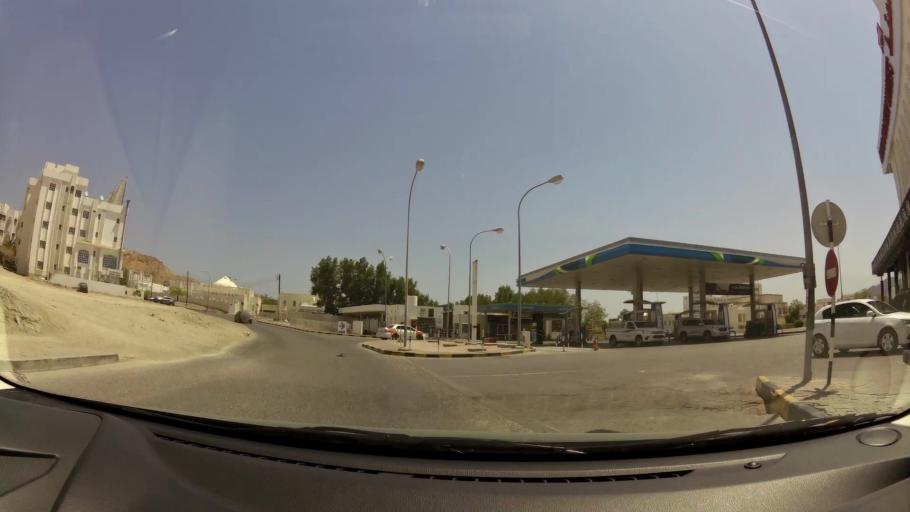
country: OM
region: Muhafazat Masqat
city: Muscat
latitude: 23.6049
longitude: 58.5362
